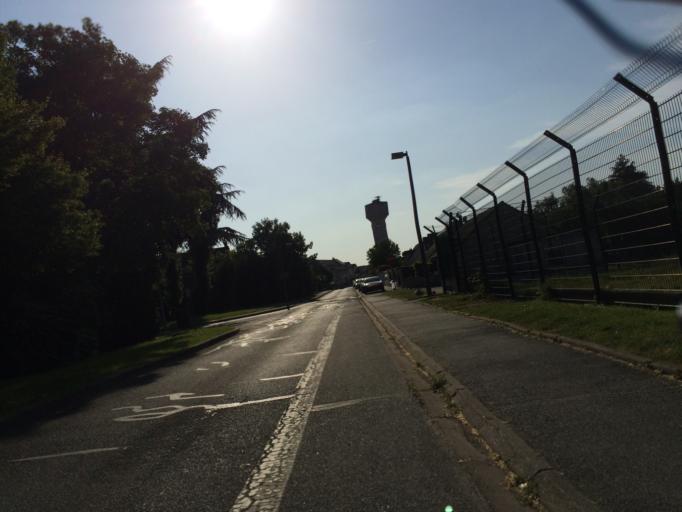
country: FR
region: Ile-de-France
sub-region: Departement de l'Essonne
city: Bondoufle
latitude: 48.6149
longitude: 2.3857
